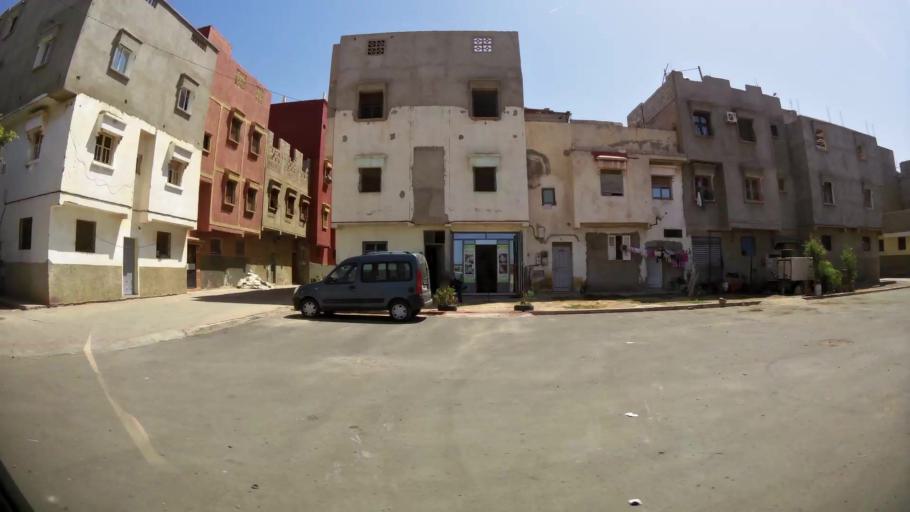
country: MA
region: Souss-Massa-Draa
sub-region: Inezgane-Ait Mellou
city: Inezgane
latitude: 30.3293
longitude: -9.5003
